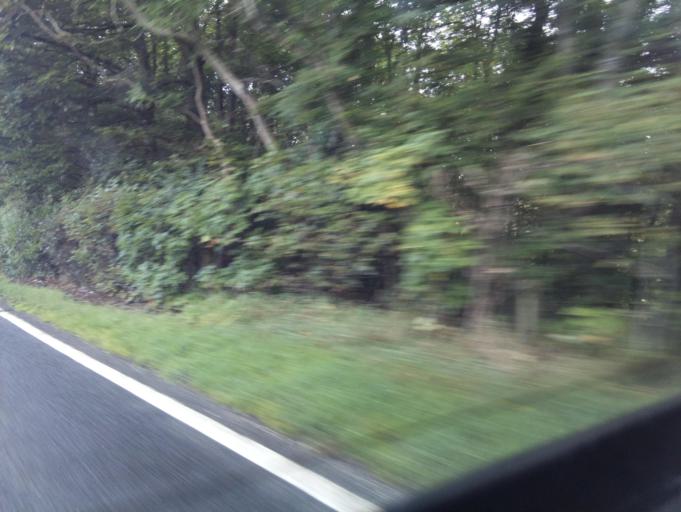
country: GB
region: Scotland
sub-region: The Scottish Borders
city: Jedburgh
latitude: 55.4112
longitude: -2.5076
